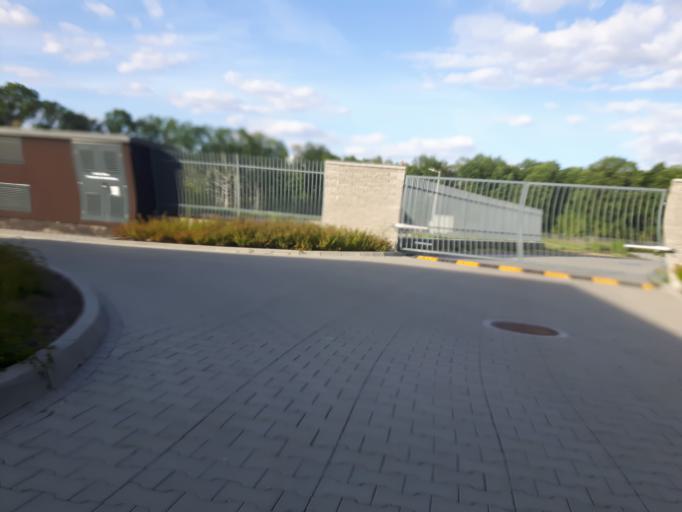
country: PL
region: Masovian Voivodeship
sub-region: Powiat wolominski
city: Zabki
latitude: 52.3000
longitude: 21.1118
